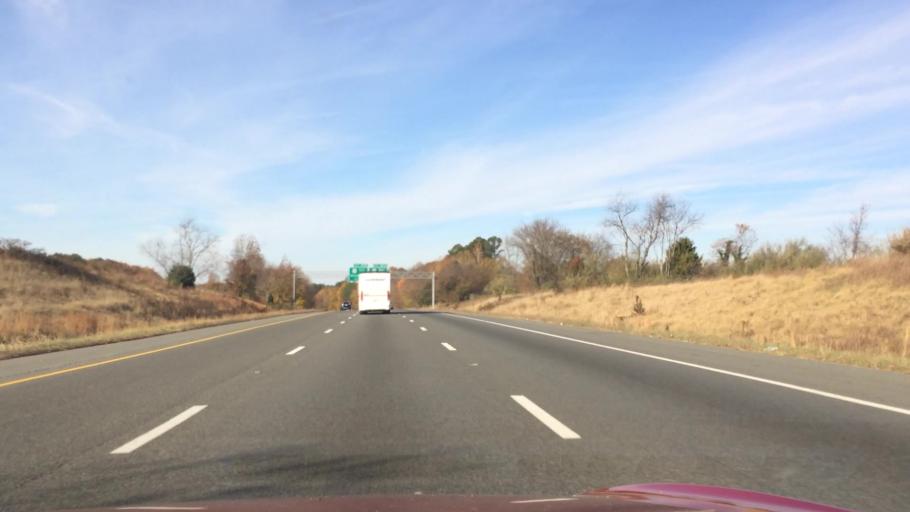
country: US
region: Virginia
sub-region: Henrico County
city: Glen Allen
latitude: 37.6821
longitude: -77.5244
